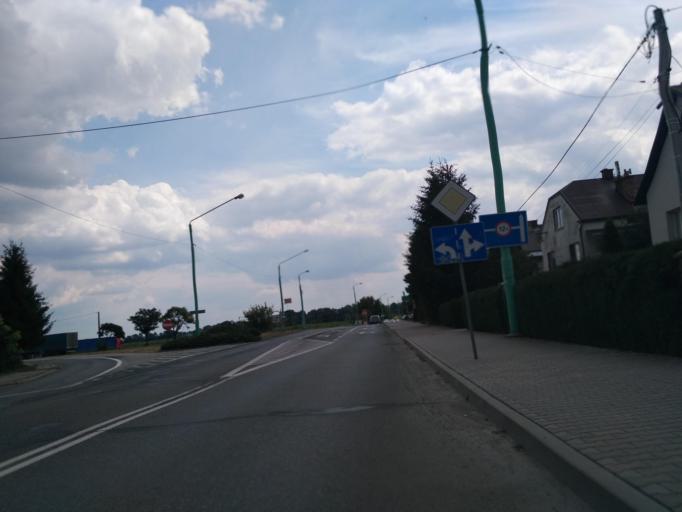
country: PL
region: Subcarpathian Voivodeship
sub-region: Powiat debicki
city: Zyrakow
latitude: 50.0637
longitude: 21.3632
